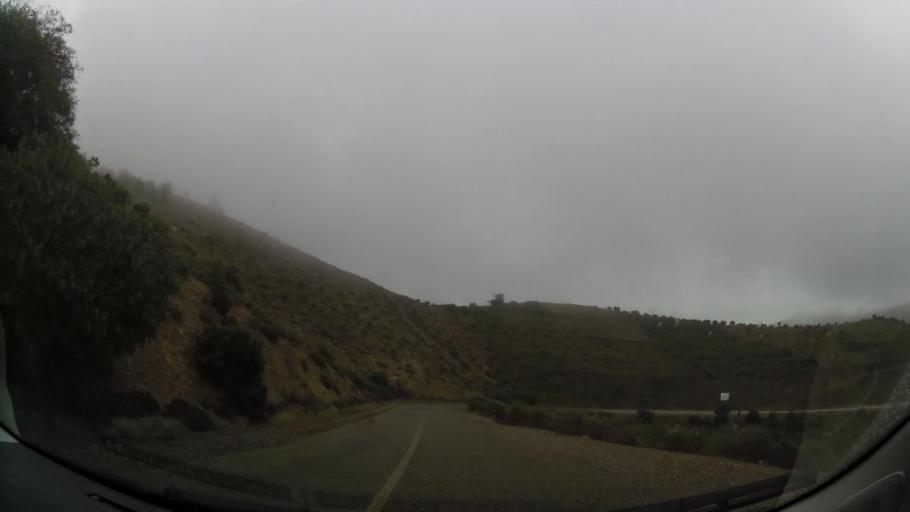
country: MA
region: Taza-Al Hoceima-Taounate
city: Imzourene
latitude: 35.1189
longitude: -3.7776
